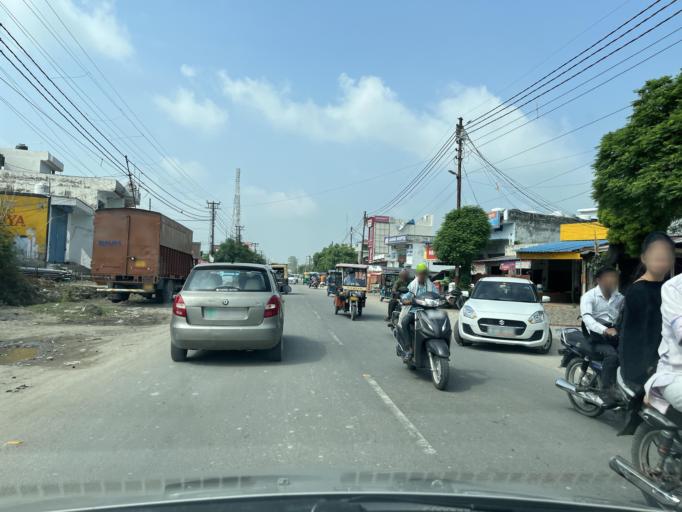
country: IN
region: Uttarakhand
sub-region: Udham Singh Nagar
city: Bazpur
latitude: 29.1558
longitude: 79.1473
